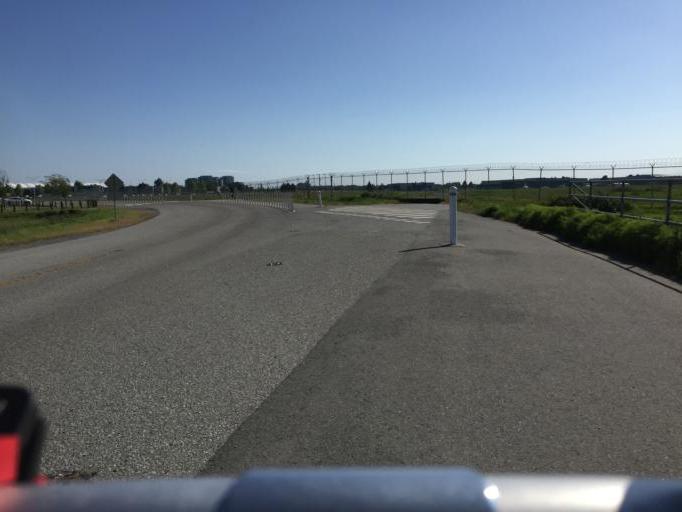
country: CA
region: British Columbia
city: Richmond
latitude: 49.1854
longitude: -123.1500
